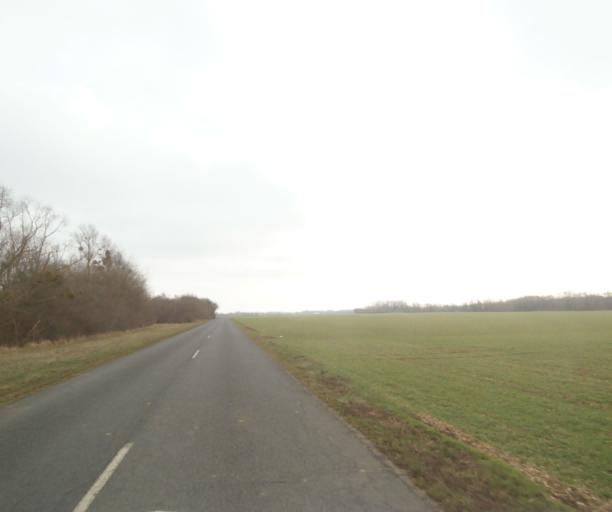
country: FR
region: Champagne-Ardenne
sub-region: Departement de la Haute-Marne
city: Villiers-en-Lieu
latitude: 48.6539
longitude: 4.7876
